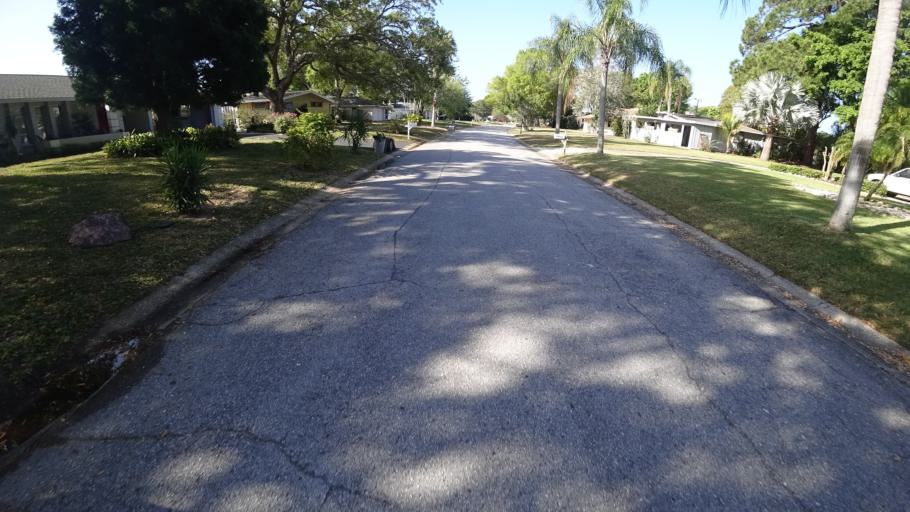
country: US
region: Florida
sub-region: Manatee County
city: Whitfield
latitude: 27.4139
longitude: -82.5604
